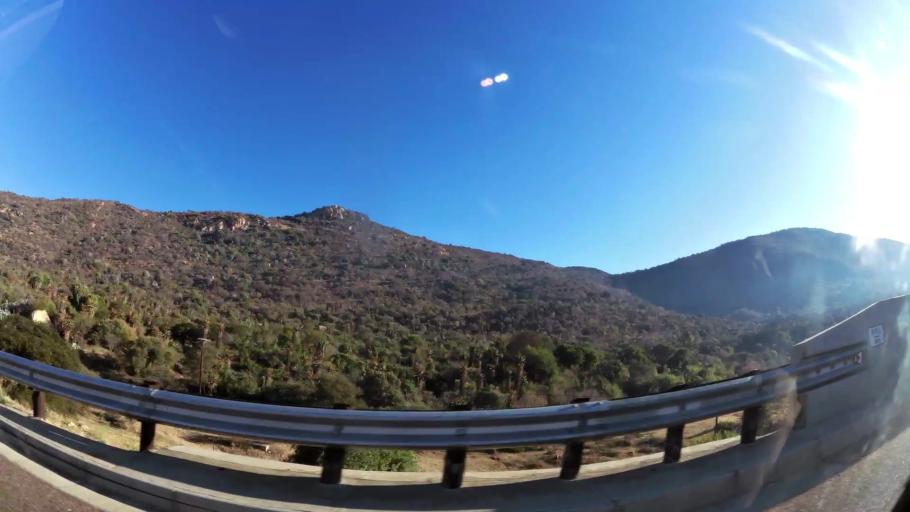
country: ZA
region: Limpopo
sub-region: Capricorn District Municipality
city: Mankoeng
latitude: -23.9426
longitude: 29.8082
